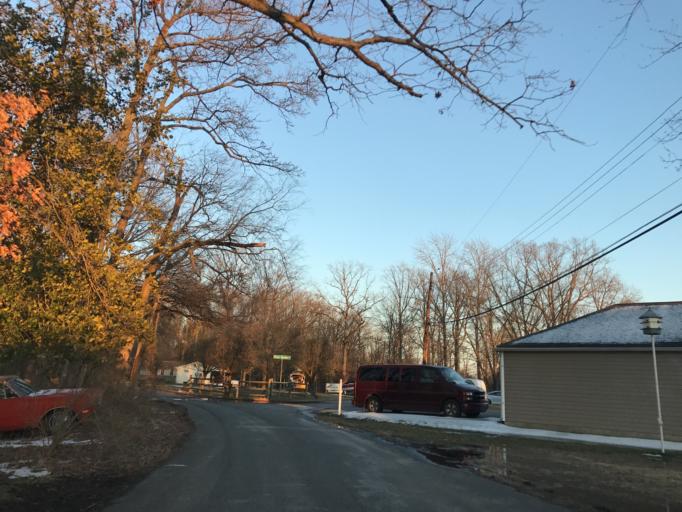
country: US
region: Maryland
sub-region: Baltimore County
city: Edgemere
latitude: 39.2825
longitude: -76.4358
